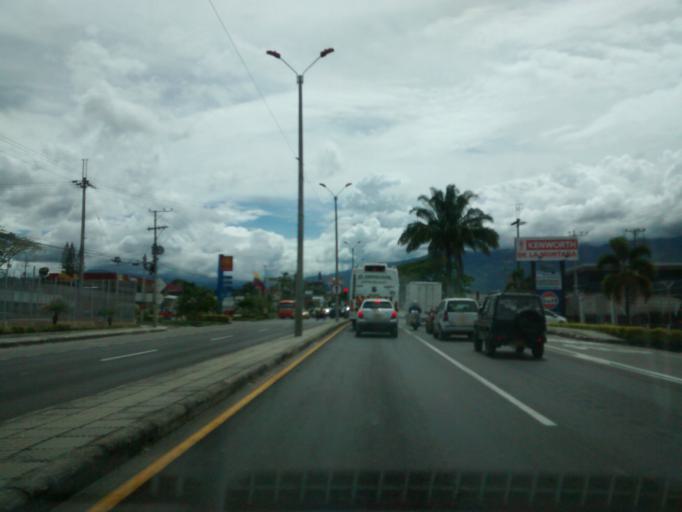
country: CO
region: Tolima
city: Ibague
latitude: 4.4069
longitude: -75.1656
